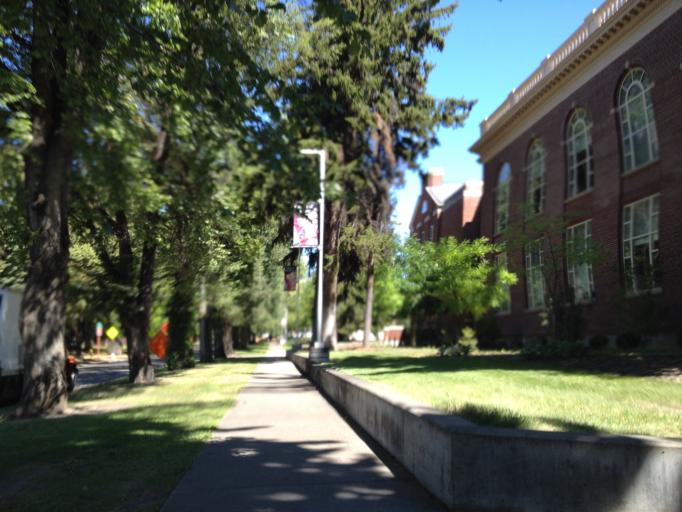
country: US
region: Washington
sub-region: Kittitas County
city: Ellensburg
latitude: 47.0000
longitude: -120.5431
